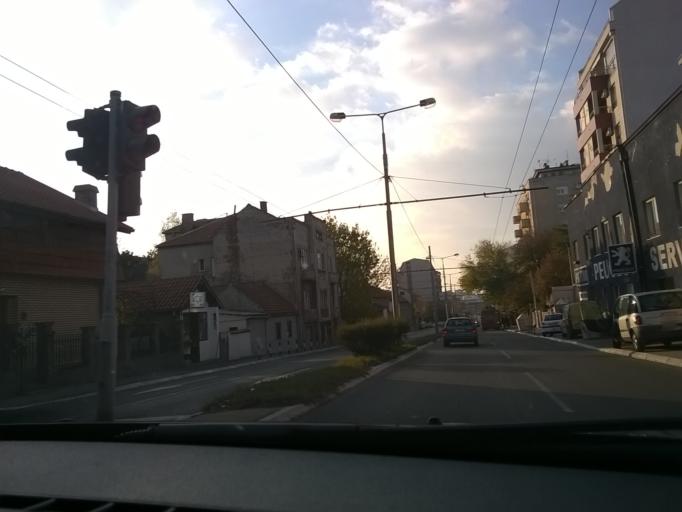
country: RS
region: Central Serbia
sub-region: Belgrade
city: Palilula
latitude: 44.8005
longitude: 20.4968
